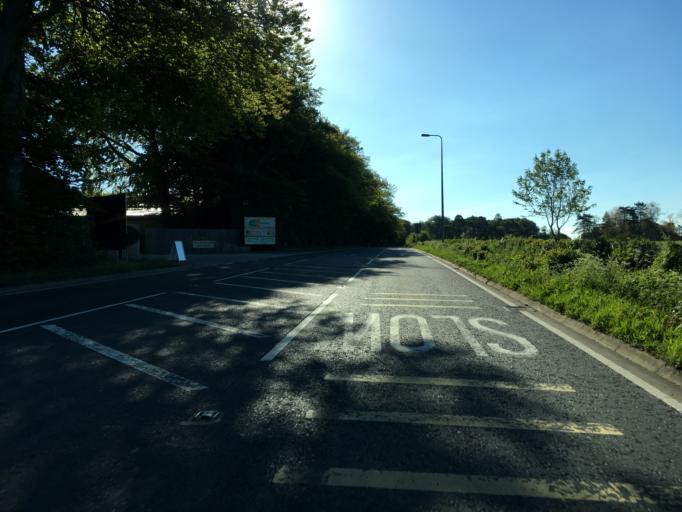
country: GB
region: England
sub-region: North Somerset
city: Easton-in-Gordano
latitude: 51.4475
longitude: -2.7143
